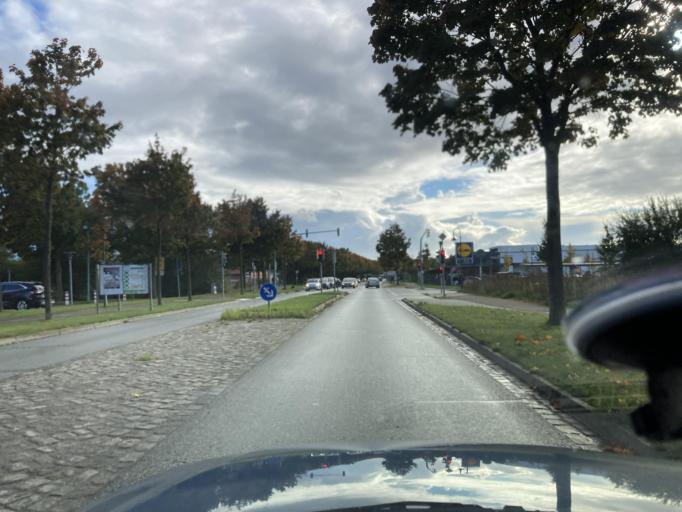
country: DE
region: Schleswig-Holstein
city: Budelsdorf
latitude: 54.3234
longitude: 9.6938
